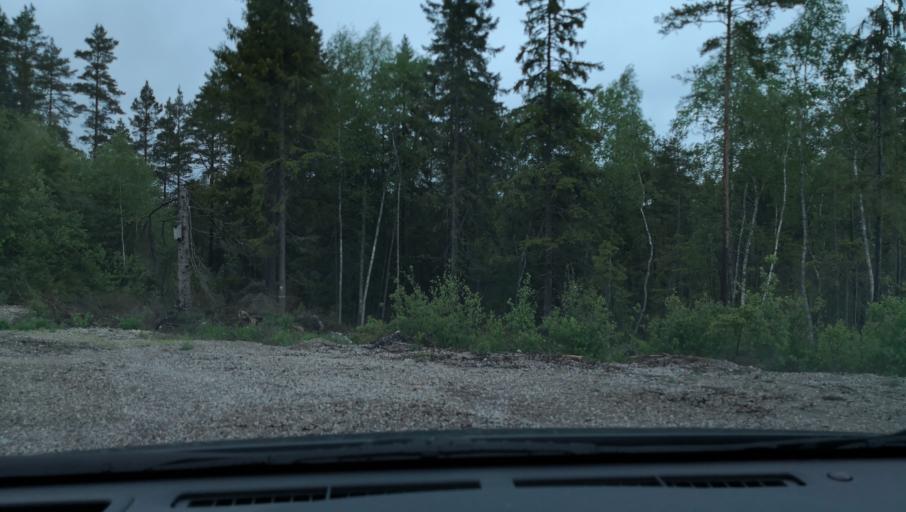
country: SE
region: Uppsala
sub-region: Enkopings Kommun
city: Orsundsbro
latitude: 59.9417
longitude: 17.3113
